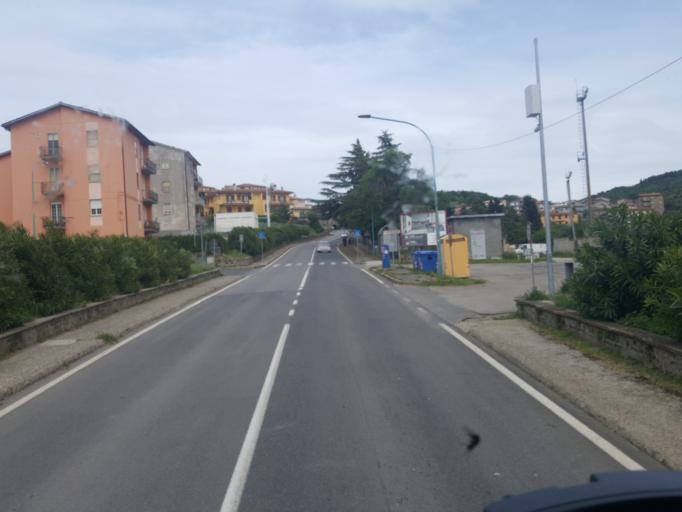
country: IT
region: Latium
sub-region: Provincia di Viterbo
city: Monte Romano
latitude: 42.2675
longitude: 11.8927
